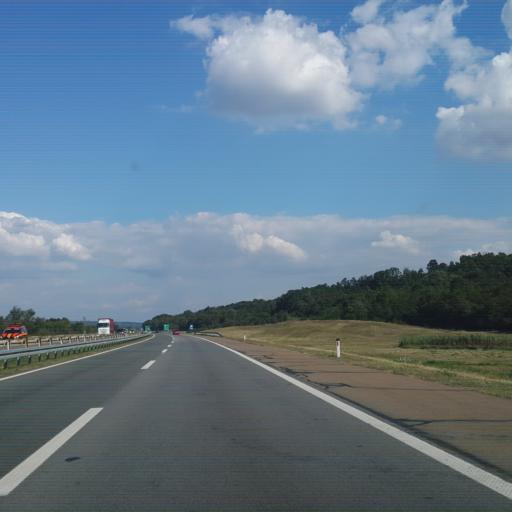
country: RS
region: Central Serbia
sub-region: Belgrade
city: Grocka
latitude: 44.5799
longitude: 20.7958
